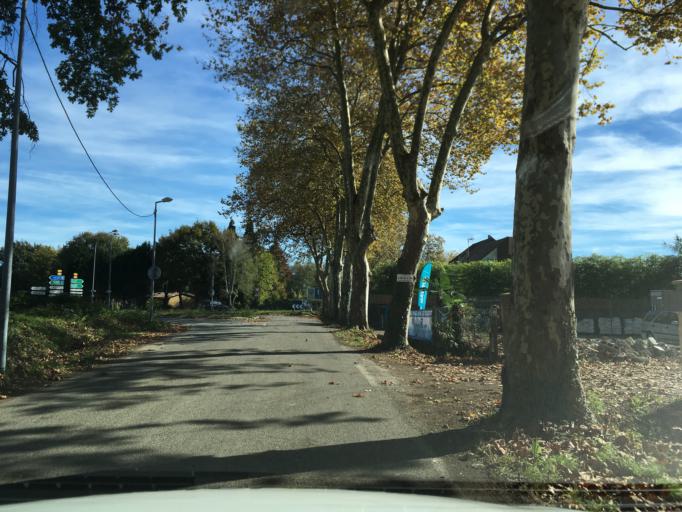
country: FR
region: Aquitaine
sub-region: Departement des Pyrenees-Atlantiques
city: Buros
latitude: 43.3233
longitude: -0.3166
